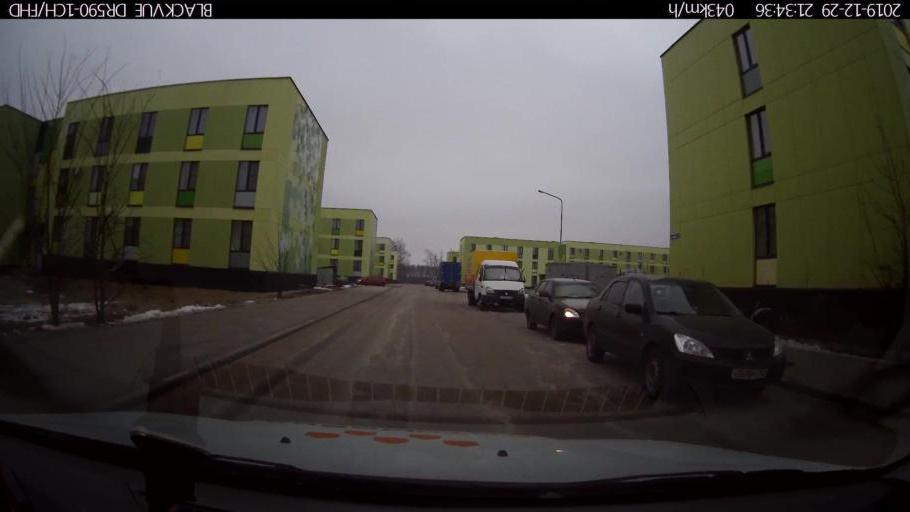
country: RU
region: Nizjnij Novgorod
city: Afonino
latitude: 56.2154
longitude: 44.0190
